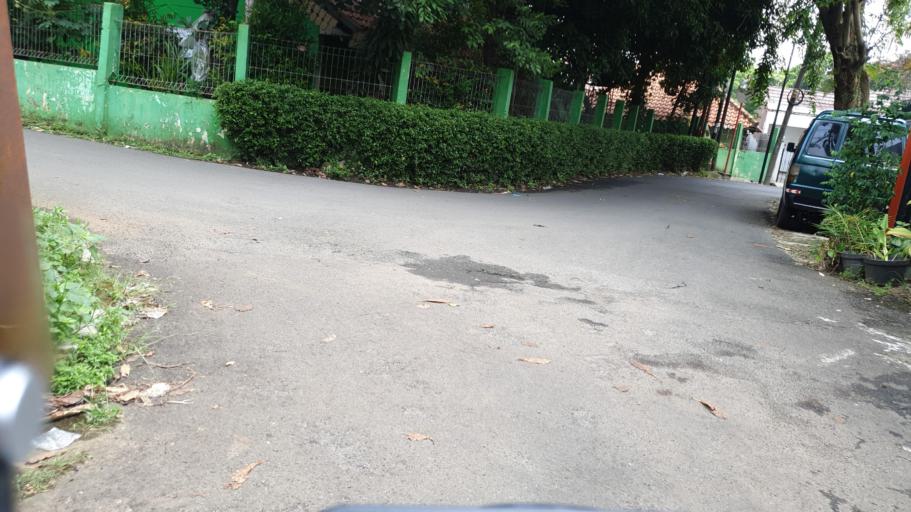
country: ID
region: West Java
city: Pamulang
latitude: -6.3041
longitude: 106.7789
